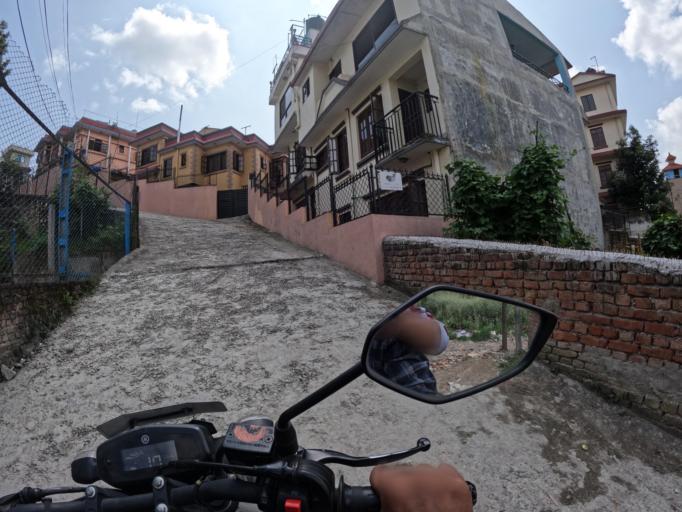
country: NP
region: Central Region
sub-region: Bagmati Zone
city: Patan
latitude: 27.6724
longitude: 85.3617
